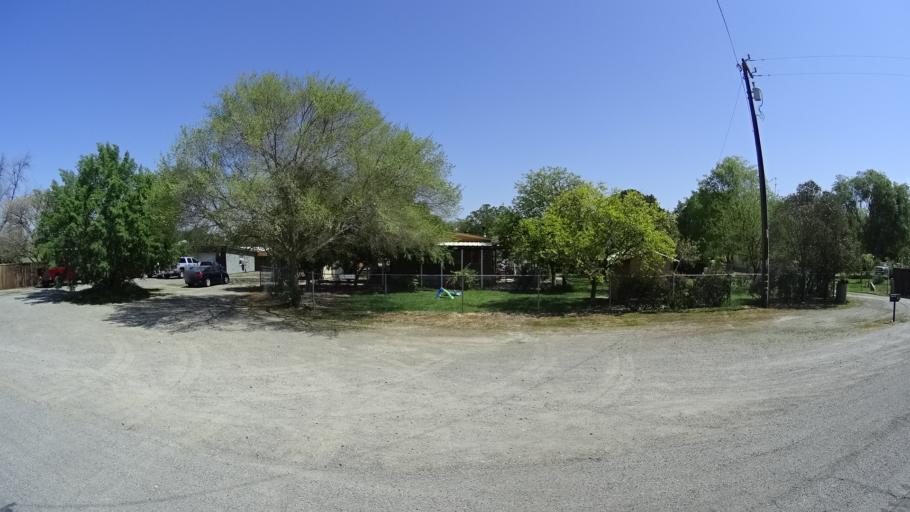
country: US
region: California
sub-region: Glenn County
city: Orland
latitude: 39.7632
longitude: -122.1968
